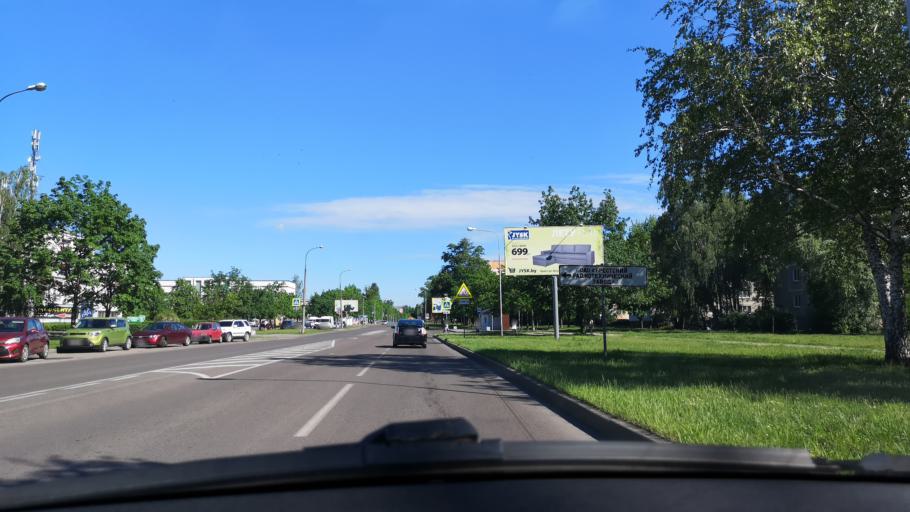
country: BY
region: Brest
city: Brest
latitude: 52.0987
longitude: 23.7523
